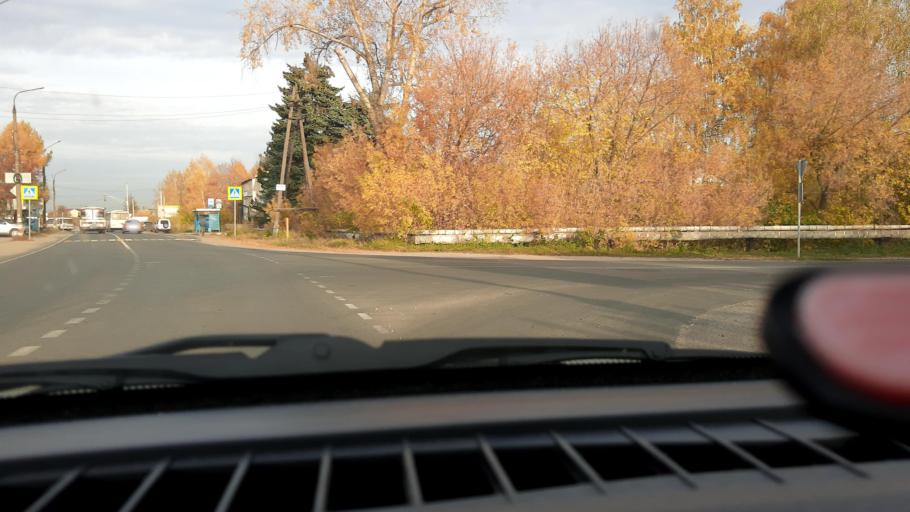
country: RU
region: Nizjnij Novgorod
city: Gorodets
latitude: 56.6460
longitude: 43.4882
